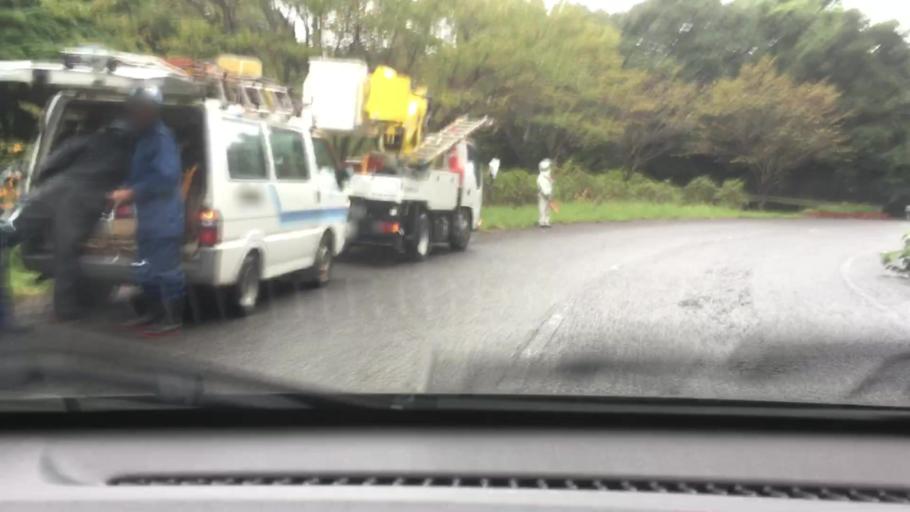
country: JP
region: Nagasaki
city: Togitsu
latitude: 32.8744
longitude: 129.7621
